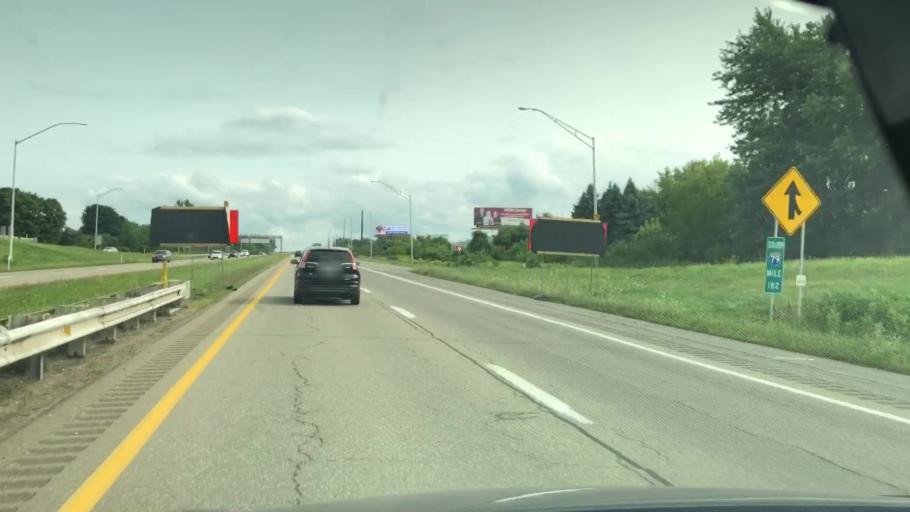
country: US
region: Pennsylvania
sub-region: Erie County
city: Erie
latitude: 42.0927
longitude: -80.1210
